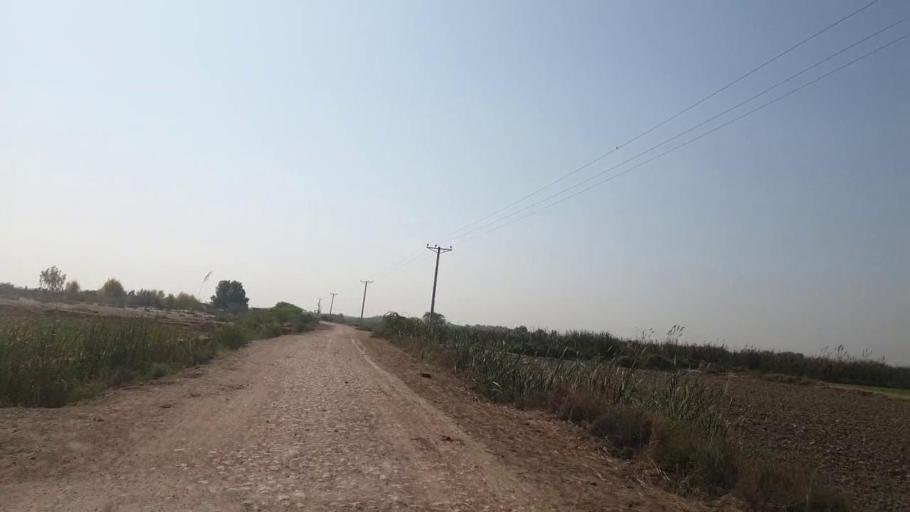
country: PK
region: Sindh
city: Thatta
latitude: 24.7301
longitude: 67.7941
